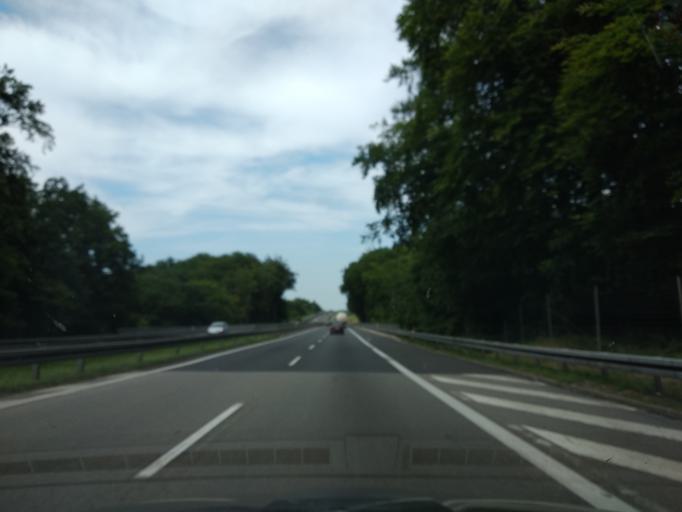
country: PL
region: West Pomeranian Voivodeship
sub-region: Szczecin
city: Szczecin
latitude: 53.3530
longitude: 14.6040
